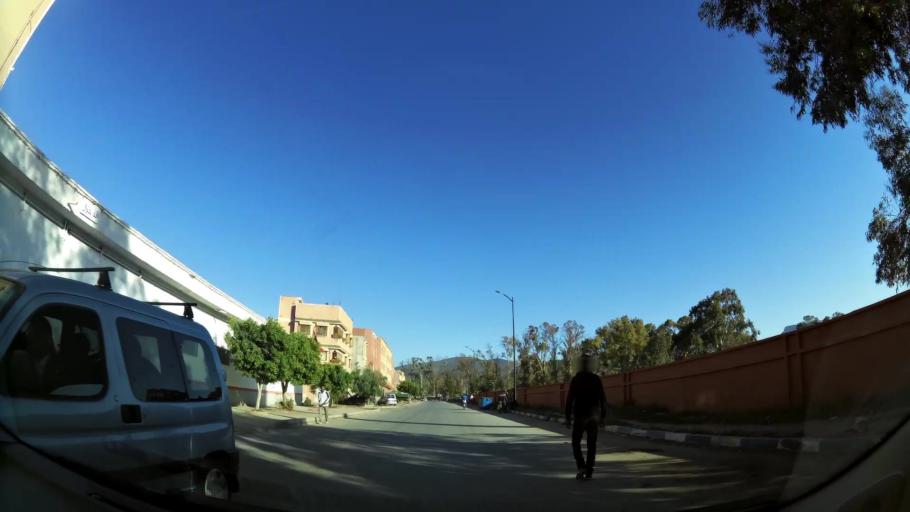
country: MA
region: Oriental
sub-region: Berkane-Taourirt
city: Berkane
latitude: 34.9251
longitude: -2.3408
